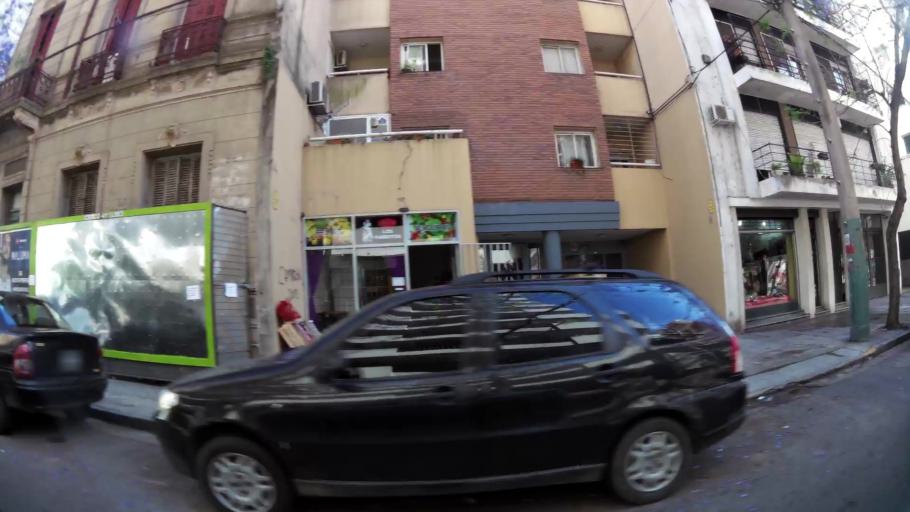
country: AR
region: Santa Fe
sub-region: Departamento de Rosario
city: Rosario
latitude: -32.9518
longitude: -60.6311
